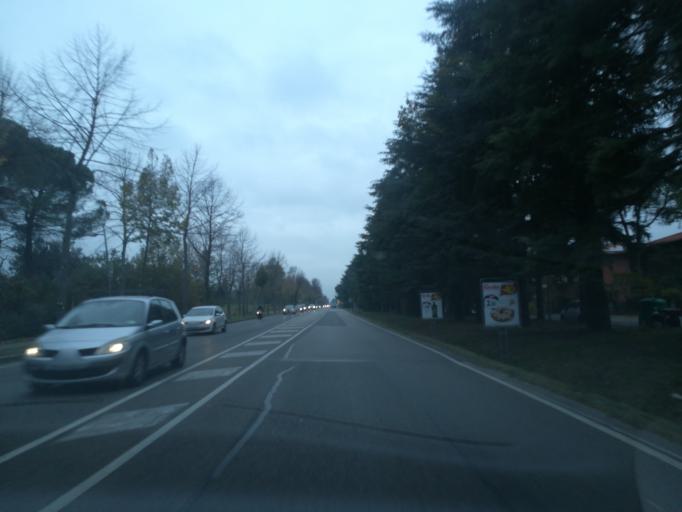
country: IT
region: Emilia-Romagna
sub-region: Provincia di Bologna
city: Imola
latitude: 44.3643
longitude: 11.6864
